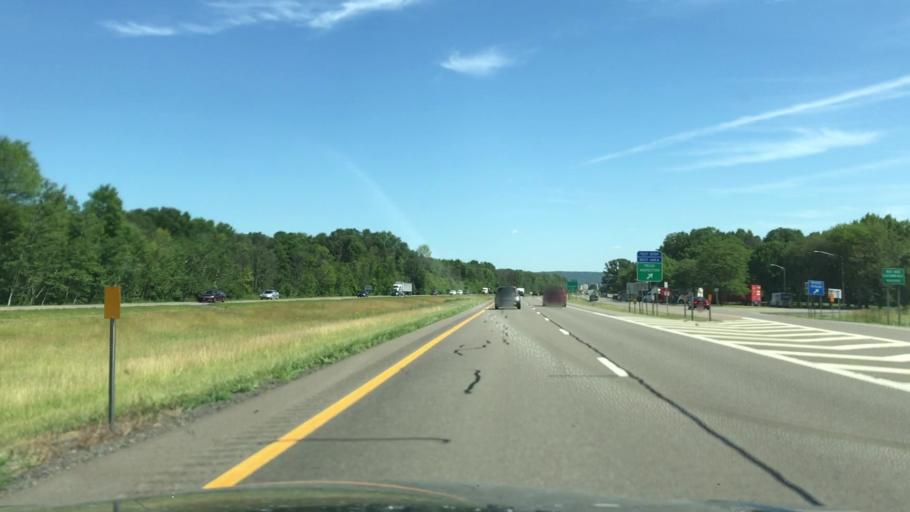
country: US
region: New York
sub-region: Steuben County
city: Gang Mills
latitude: 42.2459
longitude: -77.2002
